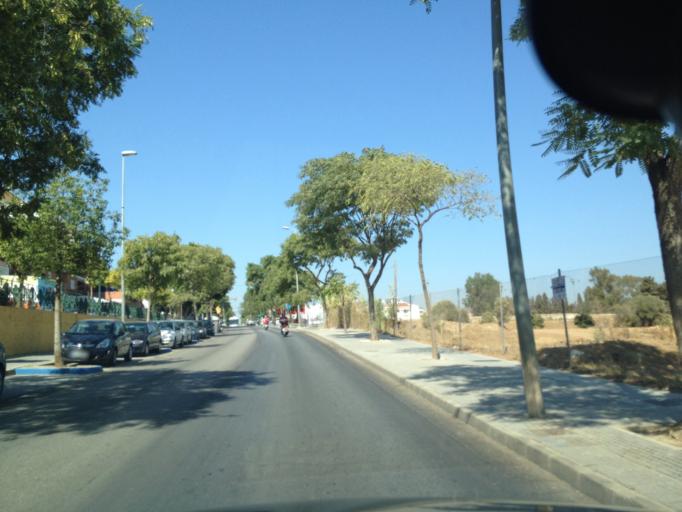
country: ES
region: Andalusia
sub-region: Provincia de Malaga
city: Alhaurin de la Torre
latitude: 36.7283
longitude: -4.5453
